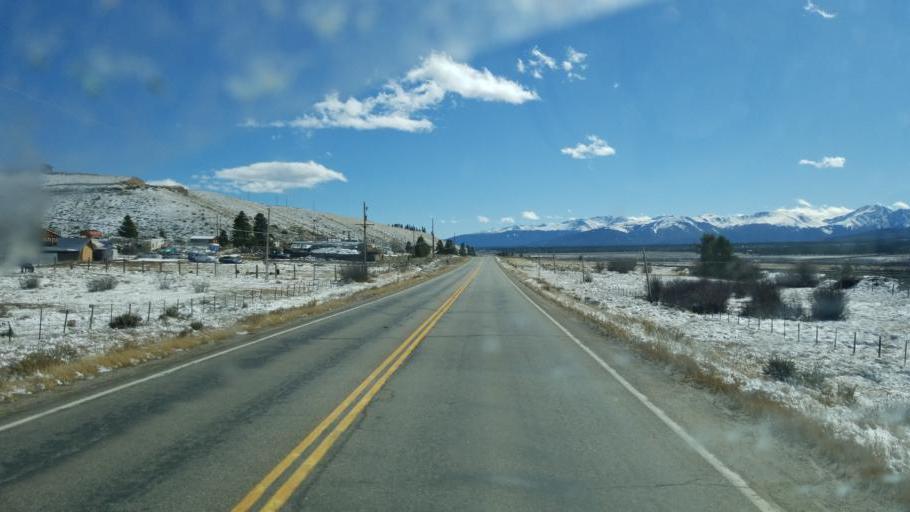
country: US
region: Colorado
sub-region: Lake County
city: Leadville North
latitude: 39.2152
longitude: -106.3472
